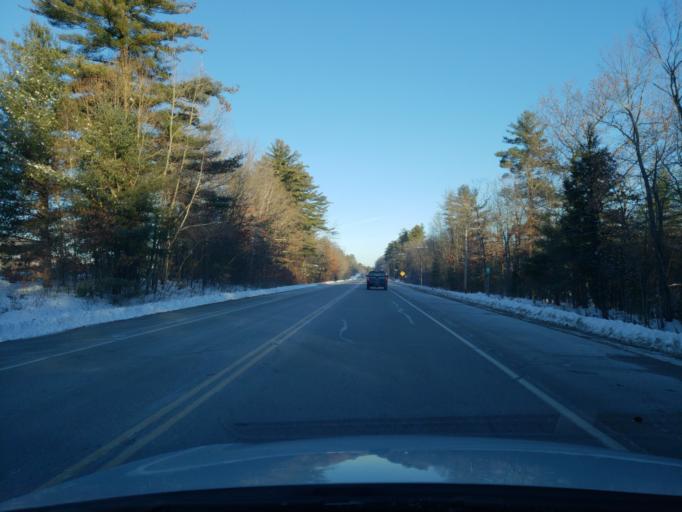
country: US
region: New Hampshire
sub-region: Hillsborough County
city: Pinardville
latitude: 42.9844
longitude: -71.5213
